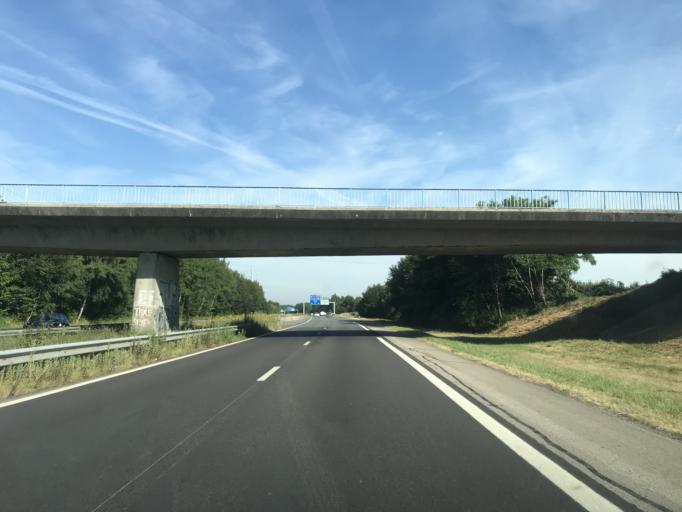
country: FR
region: Haute-Normandie
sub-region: Departement de la Seine-Maritime
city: Roumare
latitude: 49.5152
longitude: 0.9816
